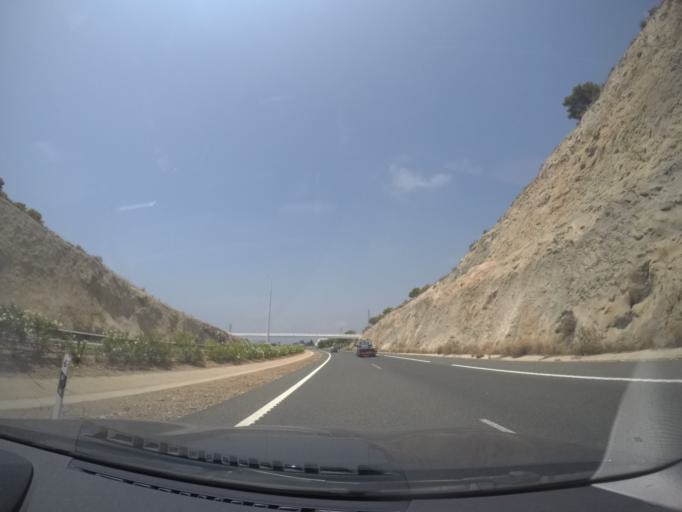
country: ES
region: Andalusia
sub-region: Provincia de Malaga
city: Nerja
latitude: 36.7603
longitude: -3.8424
